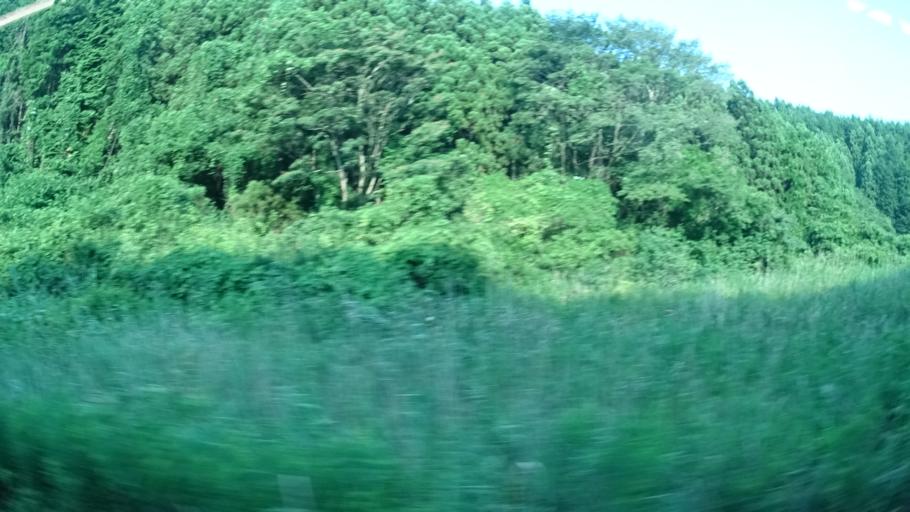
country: JP
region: Ibaraki
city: Takahagi
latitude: 36.7363
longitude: 140.7195
